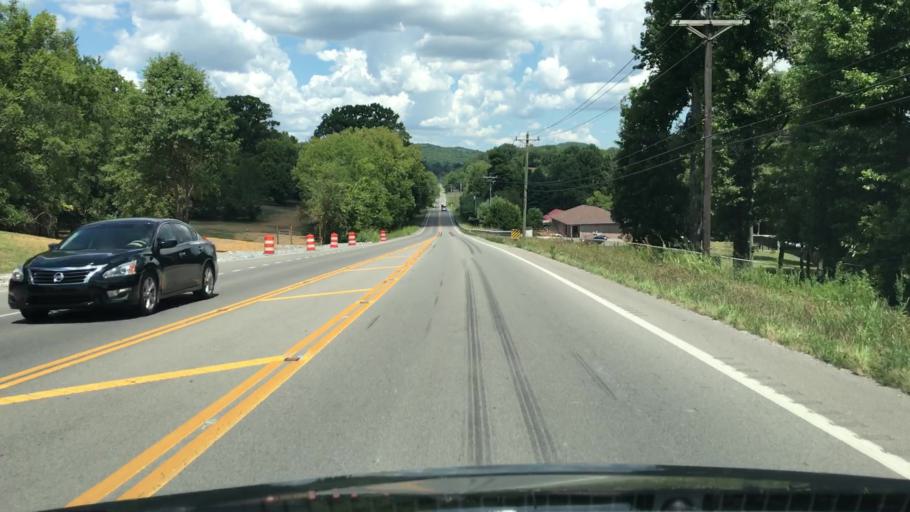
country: US
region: Tennessee
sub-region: Williamson County
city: Nolensville
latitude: 35.8792
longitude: -86.6612
